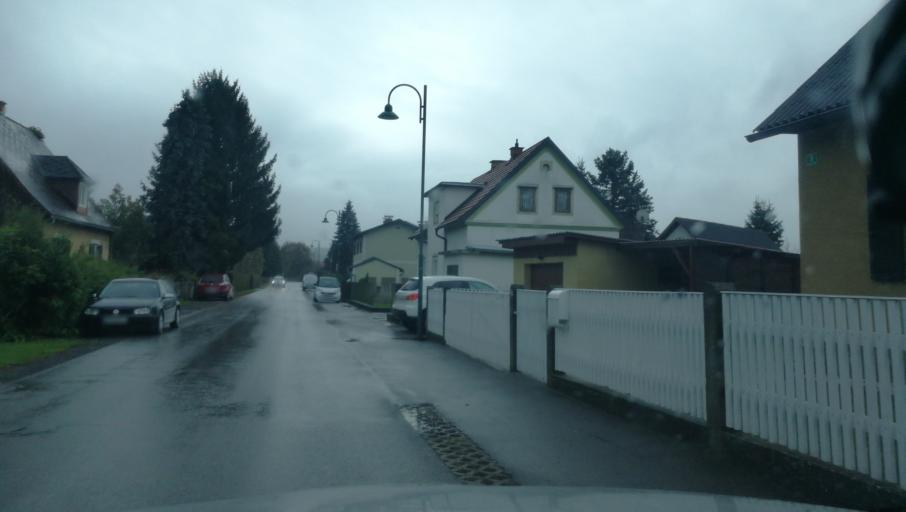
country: AT
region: Styria
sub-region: Politischer Bezirk Leibnitz
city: Strass in Steiermark
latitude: 46.7244
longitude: 15.6314
